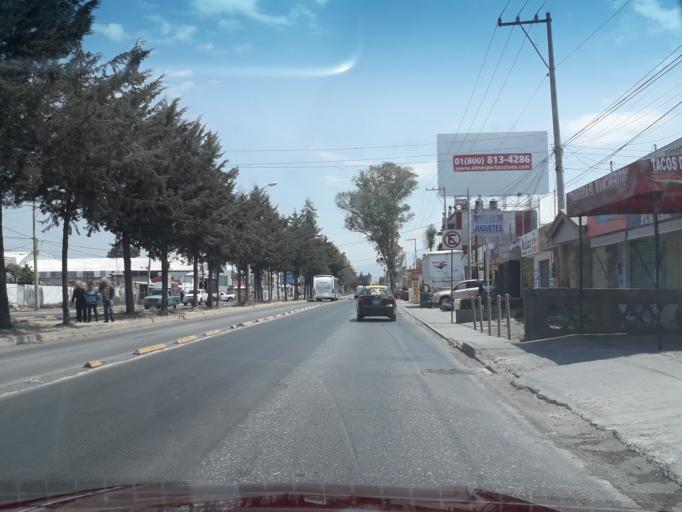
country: MX
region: Puebla
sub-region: Puebla
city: El Capulo (La Quebradora)
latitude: 18.9782
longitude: -98.2554
